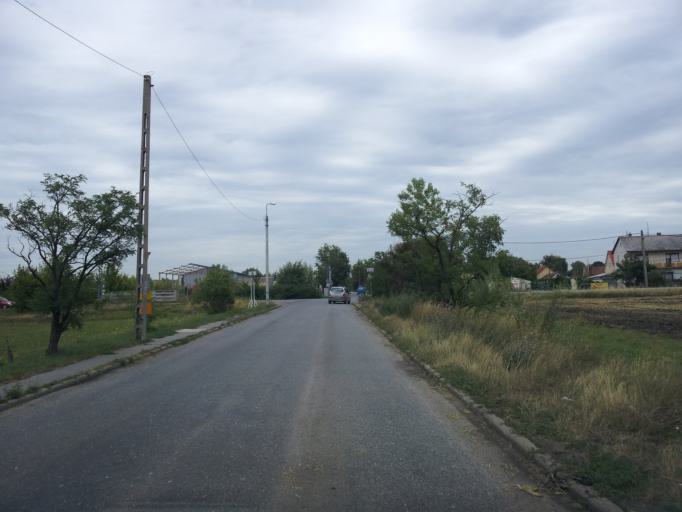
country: HU
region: Pest
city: Tarnok
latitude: 47.3734
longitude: 18.8775
